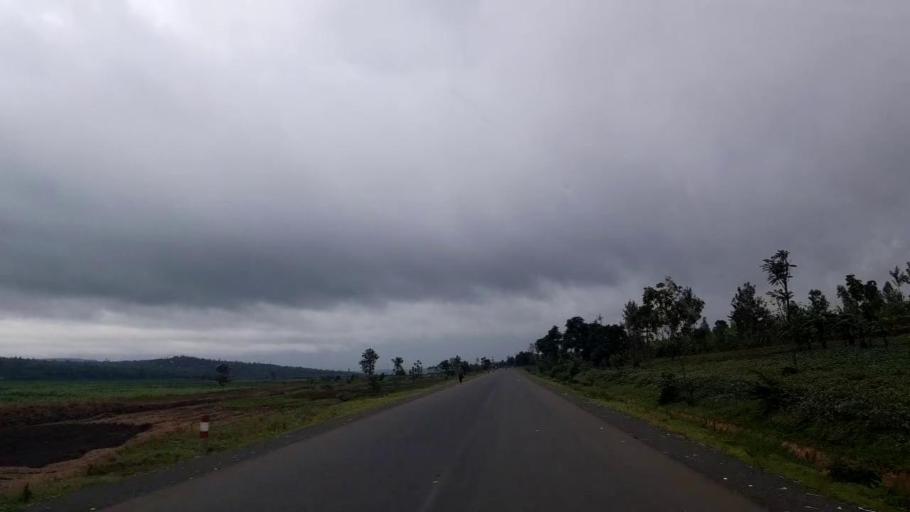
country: RW
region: Northern Province
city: Byumba
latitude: -1.4417
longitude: 30.2534
